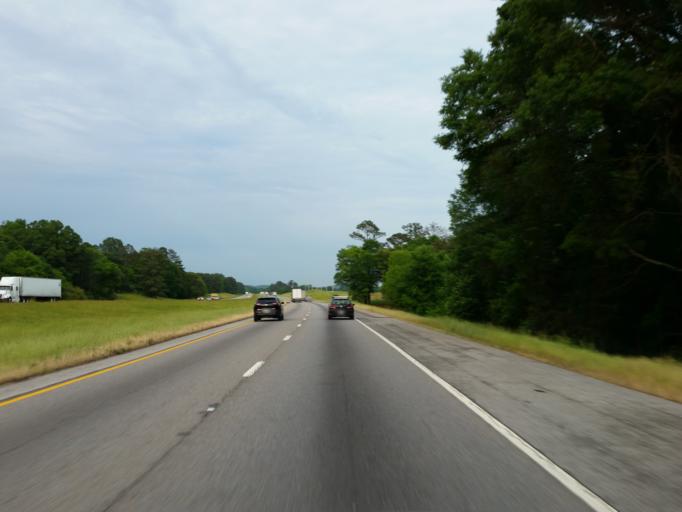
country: US
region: Alabama
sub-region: Talladega County
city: Lincoln
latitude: 33.5846
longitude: -86.0724
